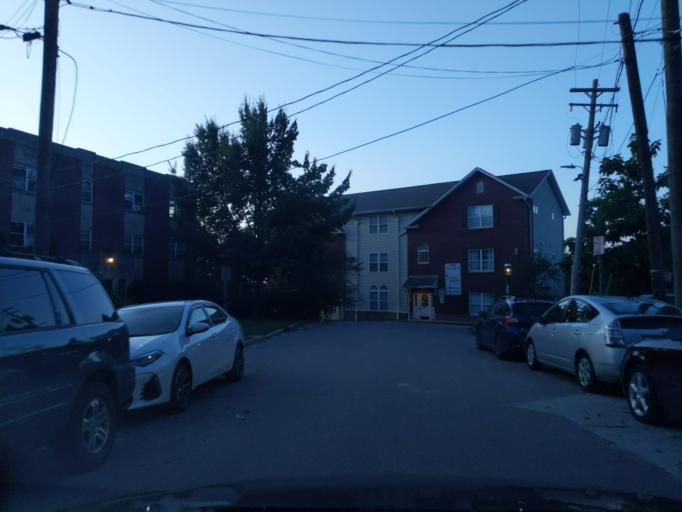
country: US
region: Ohio
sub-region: Hamilton County
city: Saint Bernard
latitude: 39.1310
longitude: -84.5240
